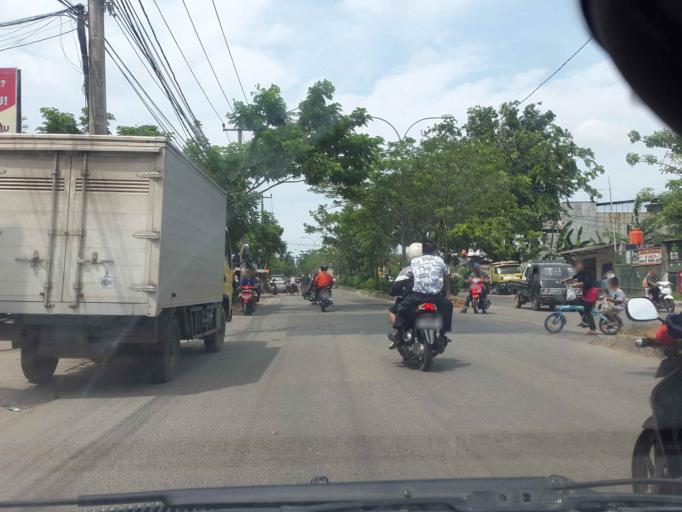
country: ID
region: Banten
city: Tangerang
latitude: -6.1473
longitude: 106.6744
